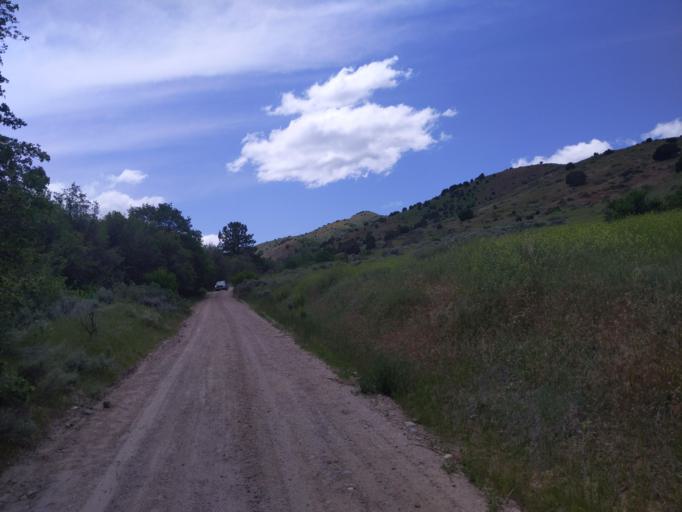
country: US
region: Idaho
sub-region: Bannock County
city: Pocatello
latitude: 42.8364
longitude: -112.4722
